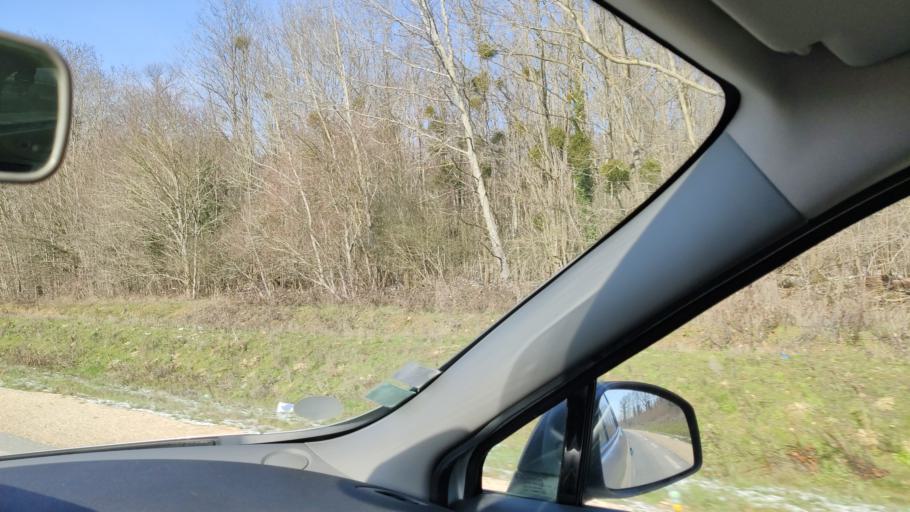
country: FR
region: Ile-de-France
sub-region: Departement de Seine-et-Marne
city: Voisenon
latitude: 48.5596
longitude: 2.6566
